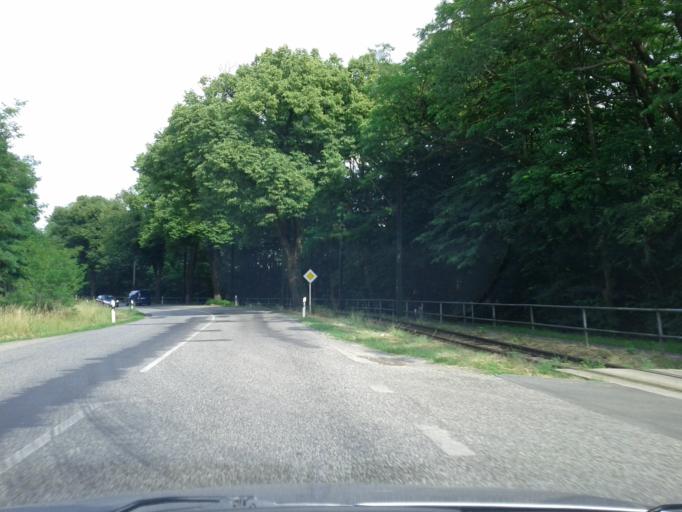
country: DE
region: Brandenburg
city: Woltersdorf
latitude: 52.4736
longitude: 13.7623
